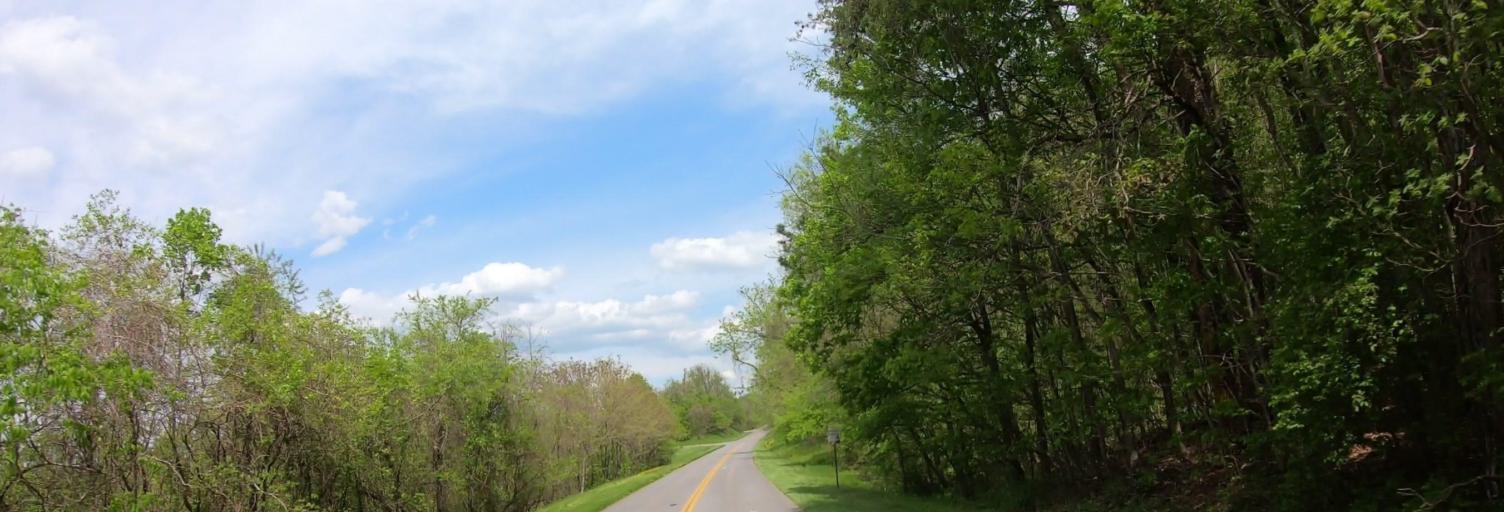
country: US
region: Virginia
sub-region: Roanoke County
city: Vinton
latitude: 37.3076
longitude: -79.8656
